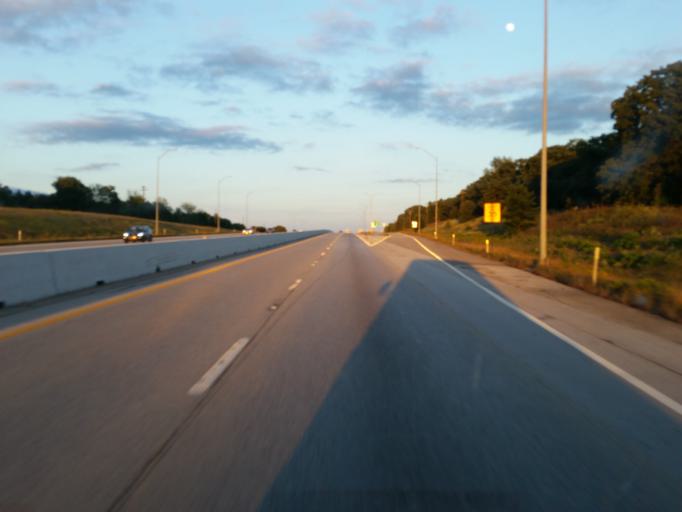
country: US
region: Texas
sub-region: Van Zandt County
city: Van
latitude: 32.4940
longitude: -95.5639
